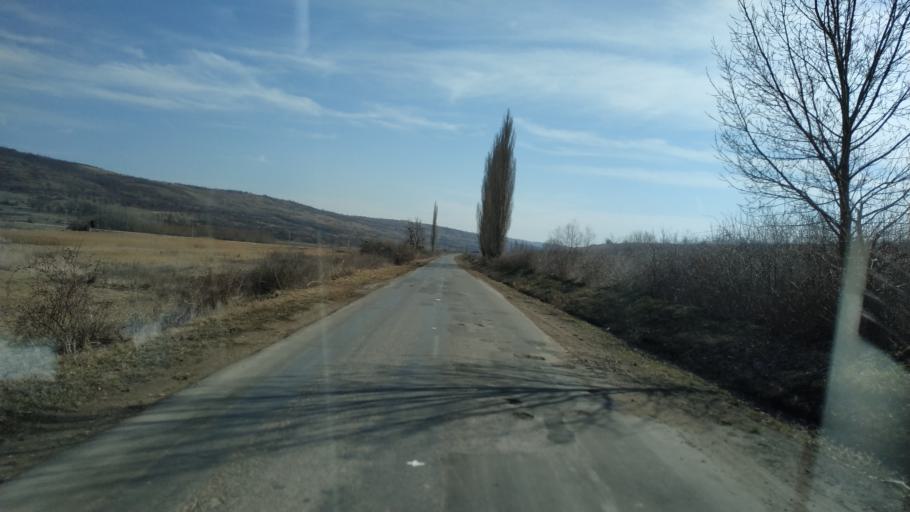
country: MD
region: Nisporeni
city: Nisporeni
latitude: 47.1694
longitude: 28.0941
